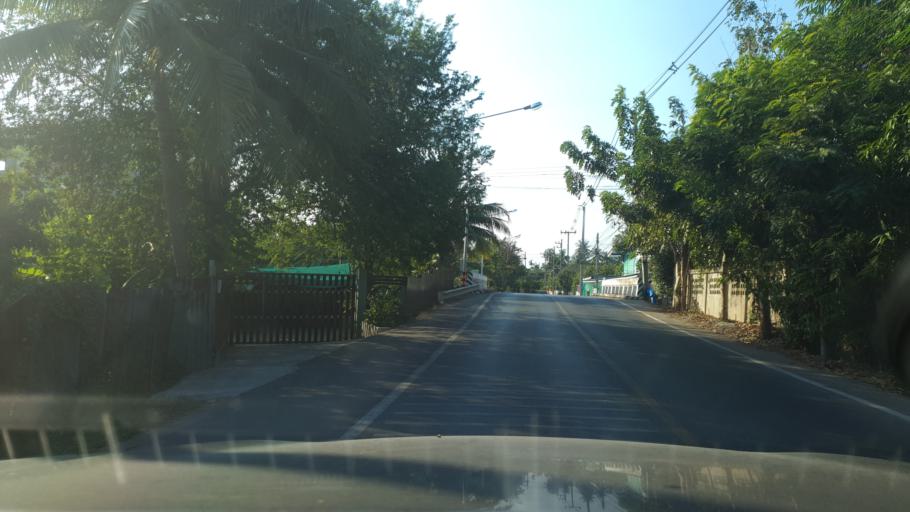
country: TH
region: Samut Songkhram
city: Amphawa
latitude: 13.4232
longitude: 99.9342
